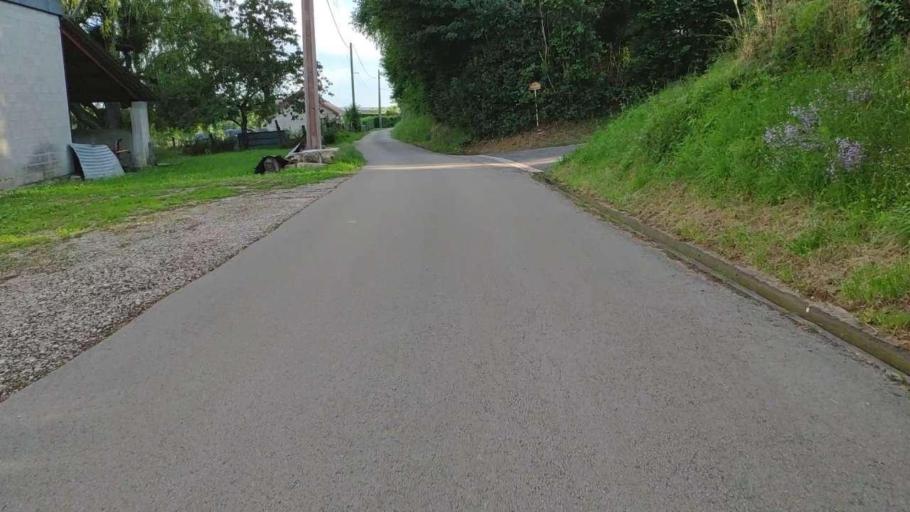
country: FR
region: Franche-Comte
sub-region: Departement du Jura
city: Bletterans
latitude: 46.7818
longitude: 5.5094
